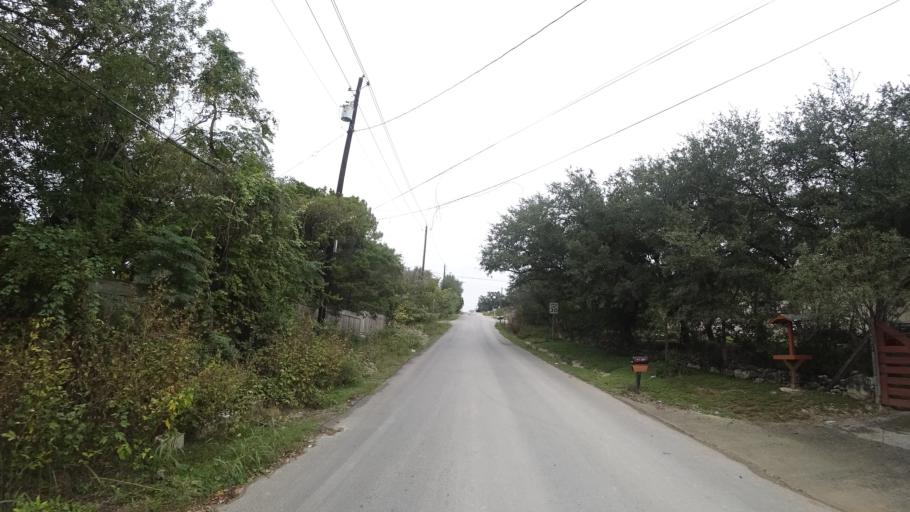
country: US
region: Texas
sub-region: Travis County
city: Hudson Bend
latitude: 30.3950
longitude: -97.9281
